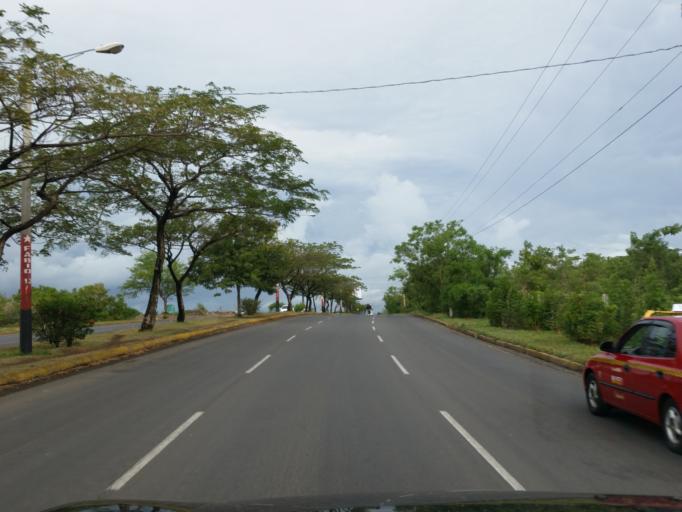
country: NI
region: Managua
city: Managua
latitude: 12.1109
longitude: -86.3042
